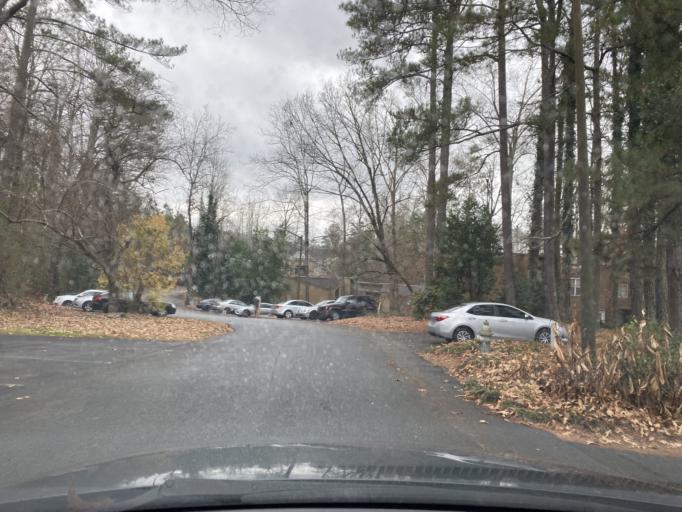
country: US
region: Georgia
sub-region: DeKalb County
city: Pine Mountain
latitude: 33.6929
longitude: -84.1470
